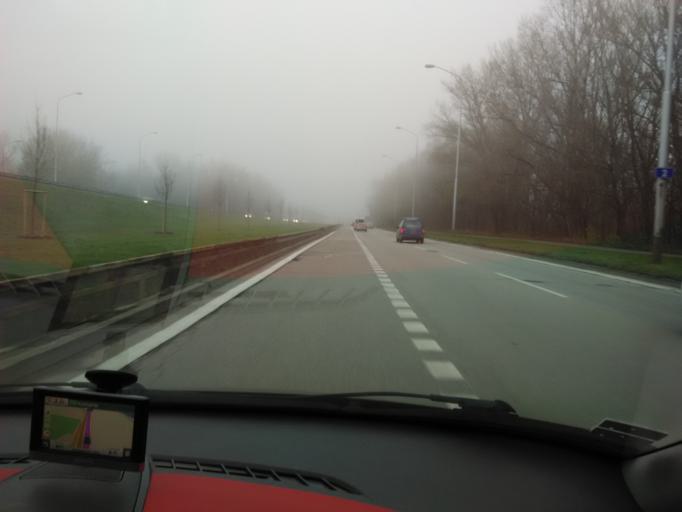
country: SK
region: Bratislavsky
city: Bratislava
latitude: 48.1129
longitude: 17.1298
